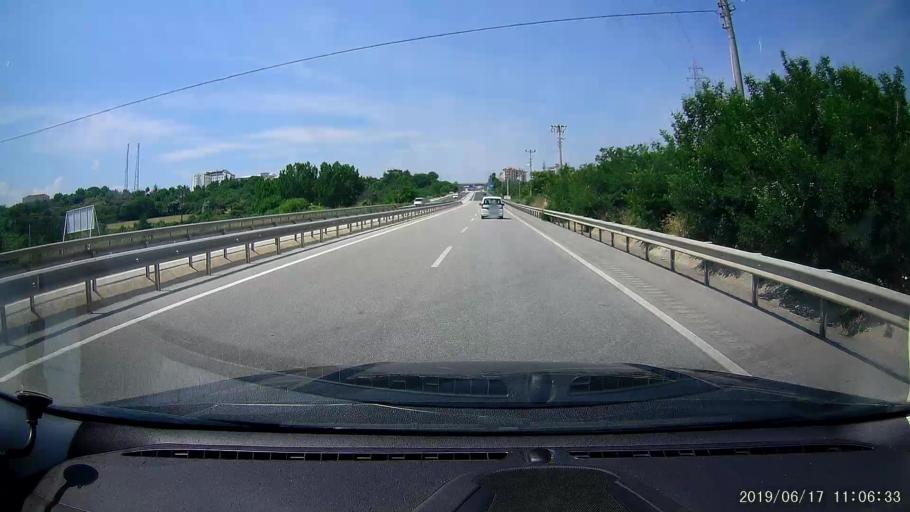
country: TR
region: Kastamonu
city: Tosya
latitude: 41.0119
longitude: 34.0657
